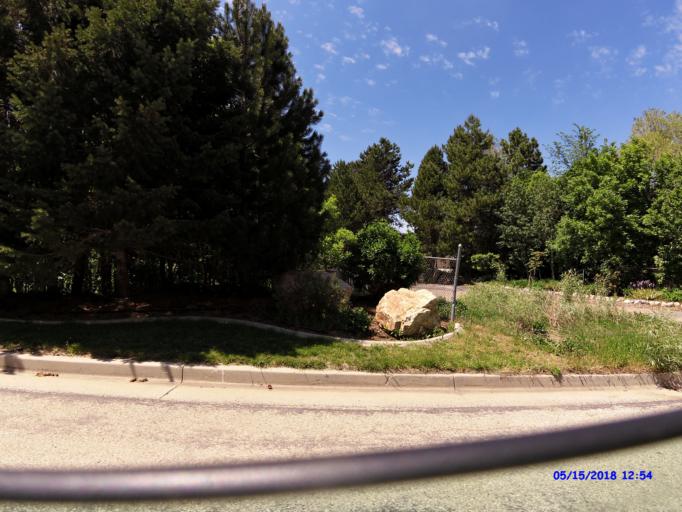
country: US
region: Utah
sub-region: Weber County
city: Uintah
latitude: 41.1589
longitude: -111.9184
